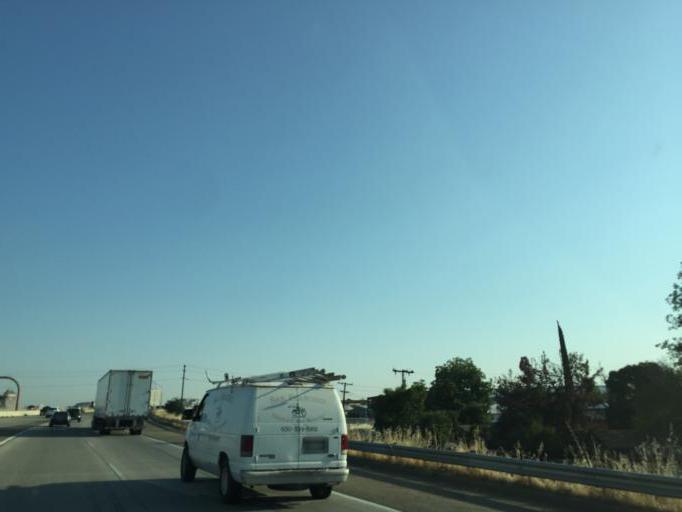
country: US
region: California
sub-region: Fresno County
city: Fresno
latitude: 36.7198
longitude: -119.7848
